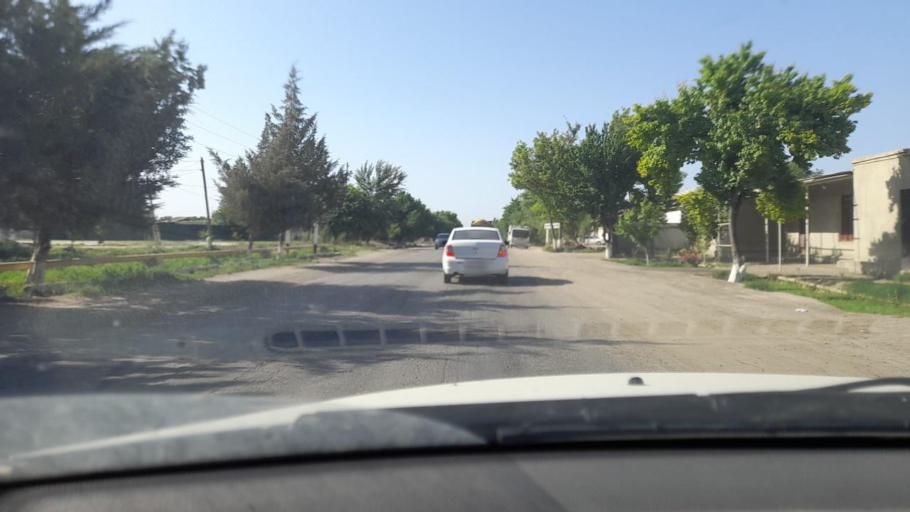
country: UZ
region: Bukhara
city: Romiton
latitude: 40.0615
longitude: 64.3275
